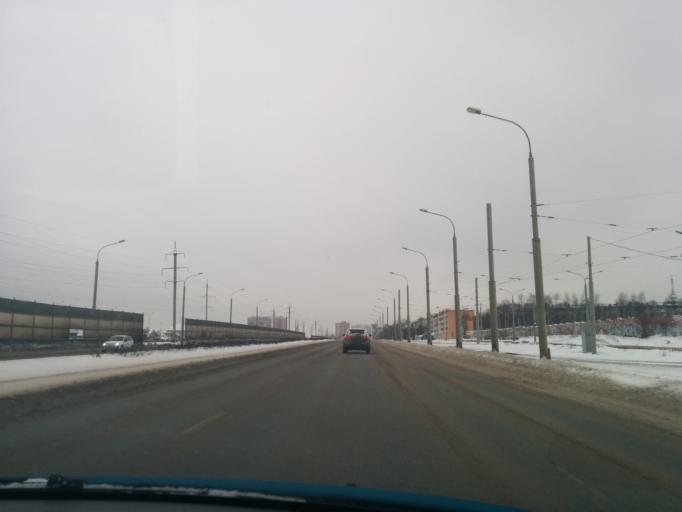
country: RU
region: Perm
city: Perm
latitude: 57.9969
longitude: 56.3083
